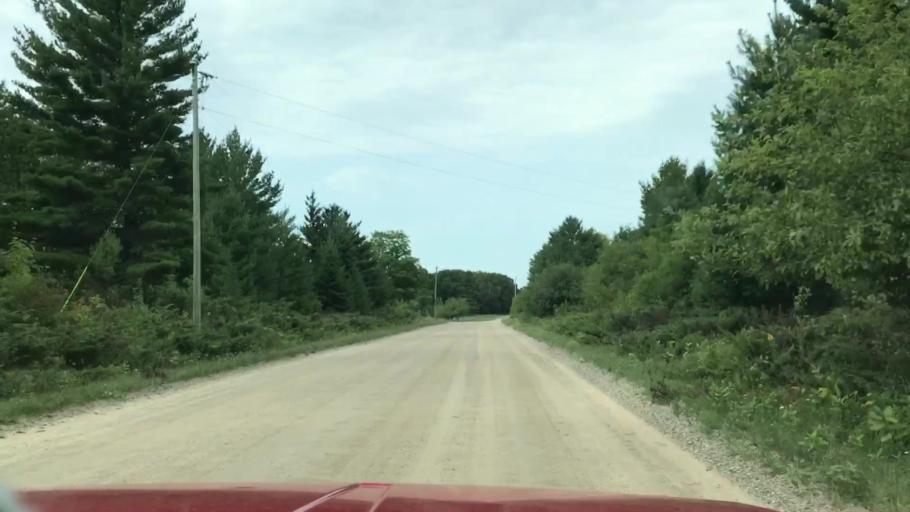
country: US
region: Michigan
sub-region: Charlevoix County
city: Charlevoix
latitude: 45.7259
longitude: -85.5502
